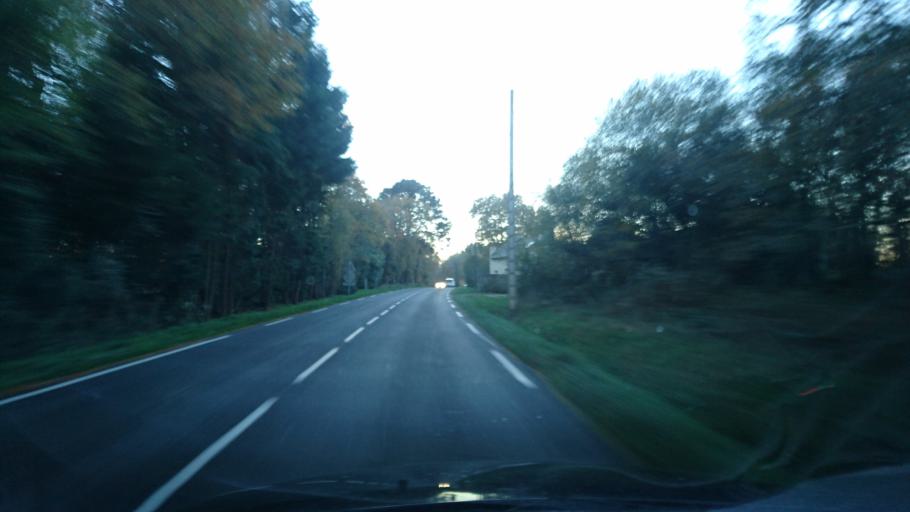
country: FR
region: Brittany
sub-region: Departement du Finistere
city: Quimperle
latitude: 47.8486
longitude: -3.5737
